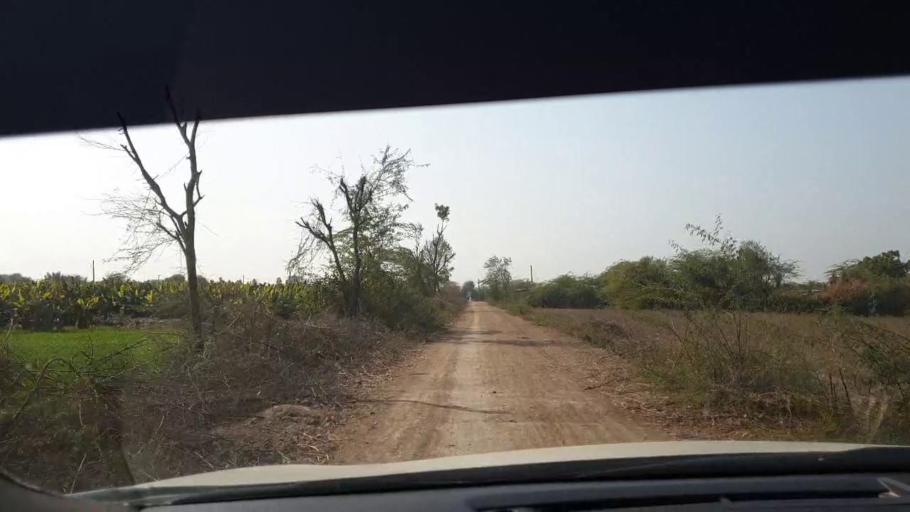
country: PK
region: Sindh
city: Tando Adam
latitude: 25.8402
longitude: 68.7158
